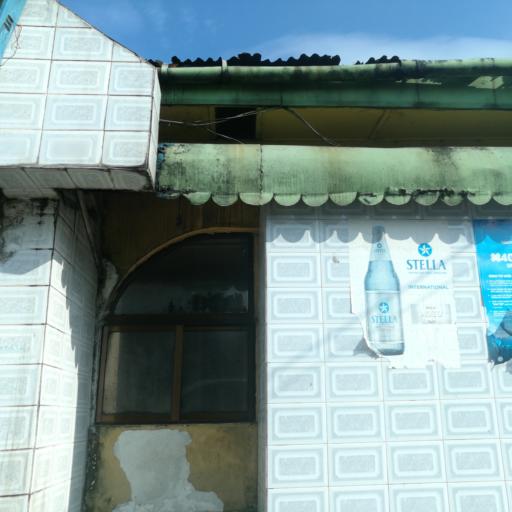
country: NG
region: Rivers
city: Port Harcourt
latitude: 4.8074
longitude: 7.0178
